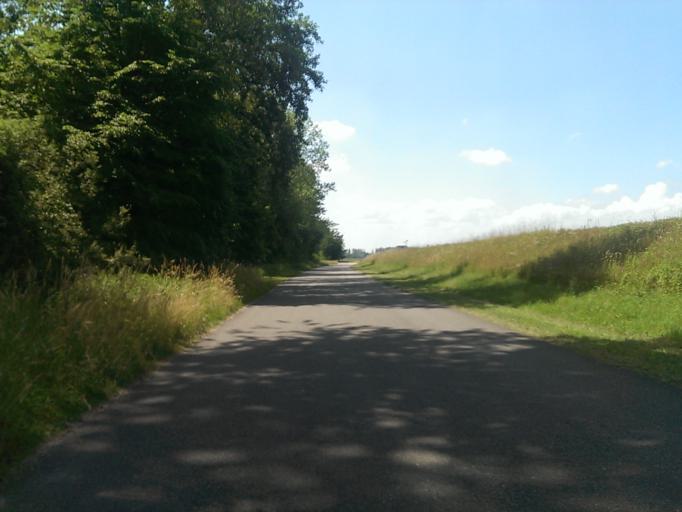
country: DE
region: Baden-Wuerttemberg
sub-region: Karlsruhe Region
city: Greffern
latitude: 48.7577
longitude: 7.9974
